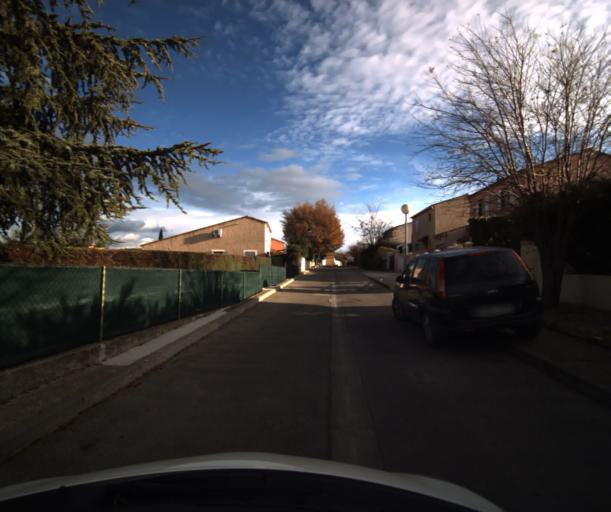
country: FR
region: Provence-Alpes-Cote d'Azur
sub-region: Departement du Vaucluse
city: Pertuis
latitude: 43.6934
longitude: 5.5286
